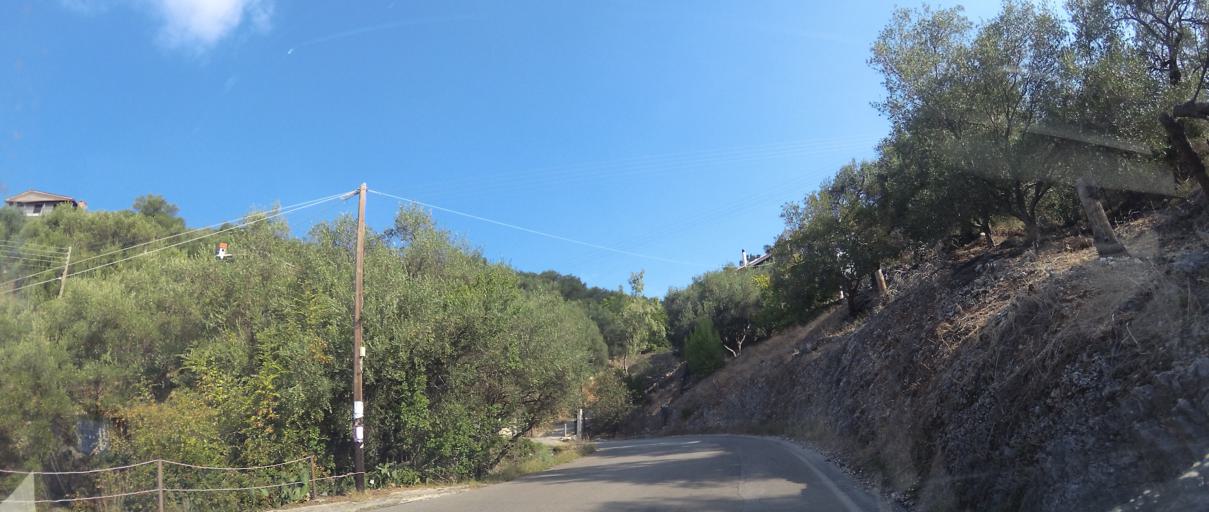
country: GR
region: Ionian Islands
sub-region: Nomos Kerkyras
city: Kontokali
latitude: 39.7091
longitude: 19.8465
